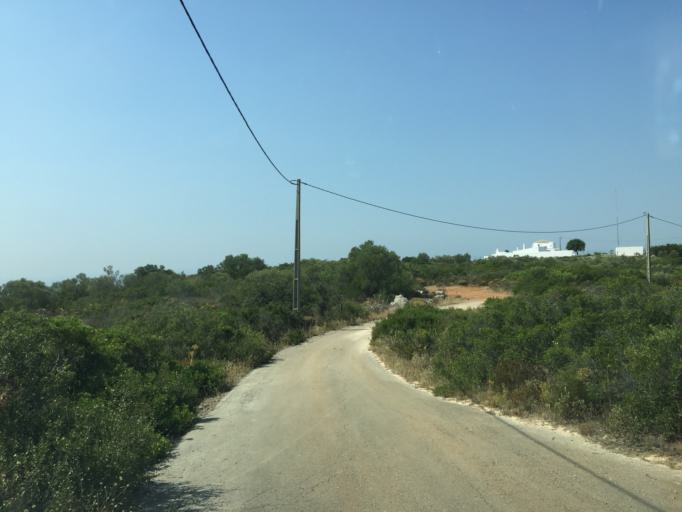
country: PT
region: Faro
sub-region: Faro
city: Santa Barbara de Nexe
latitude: 37.1127
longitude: -7.9795
